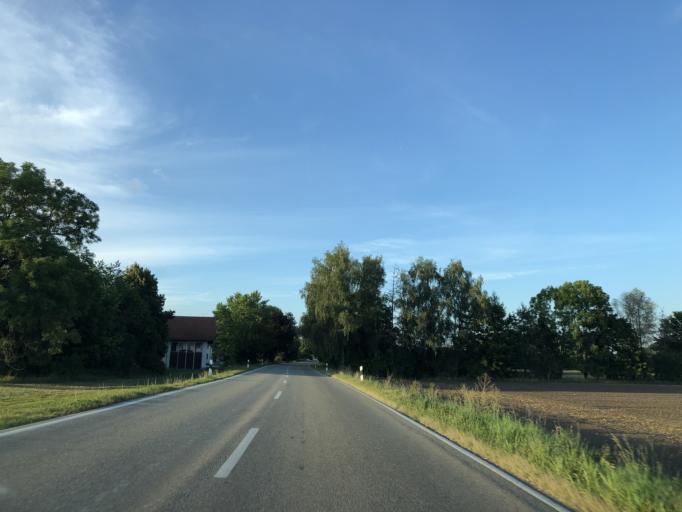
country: DE
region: Bavaria
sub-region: Upper Bavaria
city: Finsing
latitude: 48.2359
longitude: 11.8162
